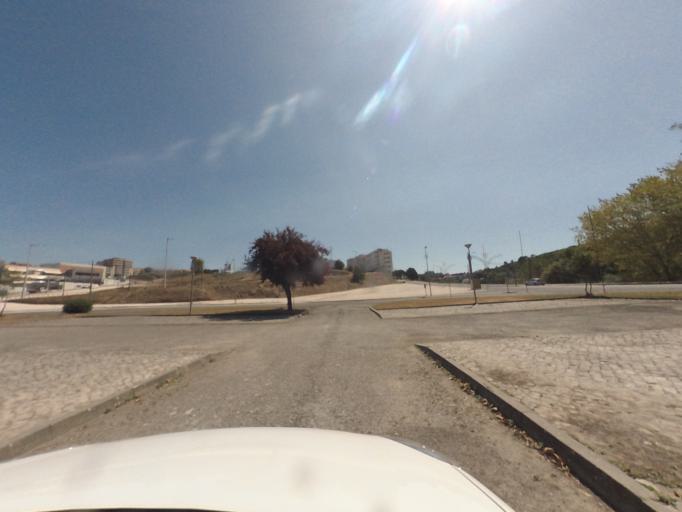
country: PT
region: Leiria
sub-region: Alcobaca
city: Alcobaca
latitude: 39.5579
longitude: -8.9803
